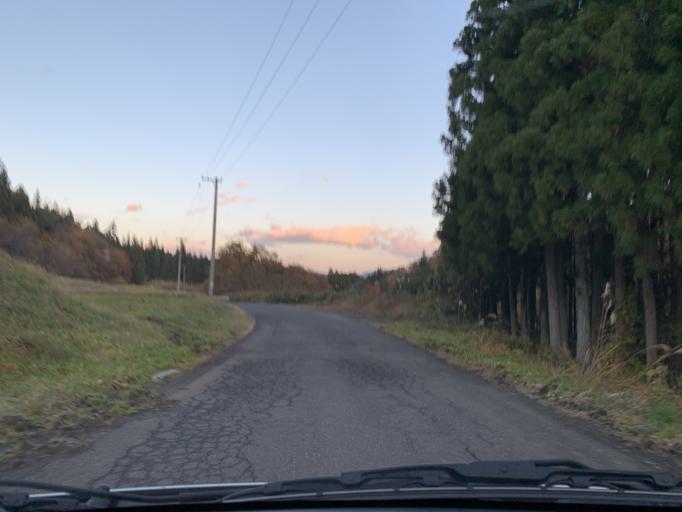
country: JP
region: Iwate
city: Ichinoseki
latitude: 39.0119
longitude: 141.0700
